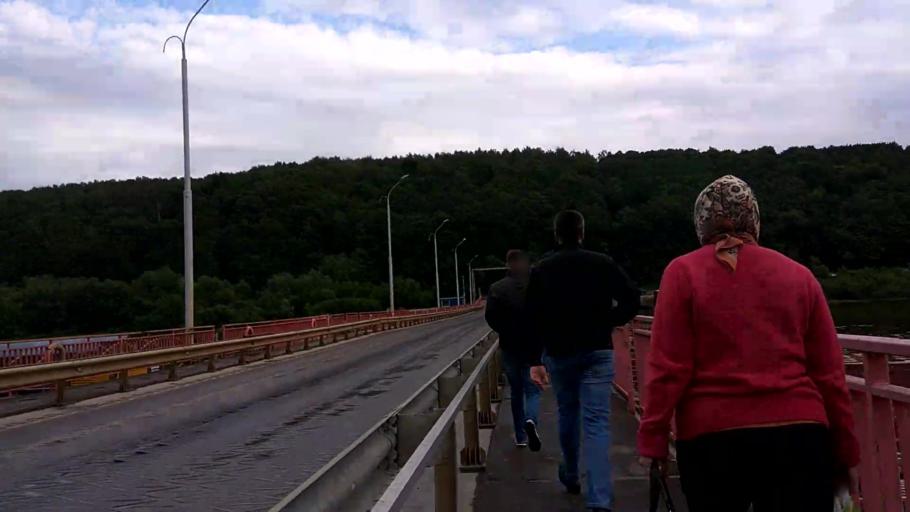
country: RU
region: Moskovskaya
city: Ozery
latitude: 54.8351
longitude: 38.5840
